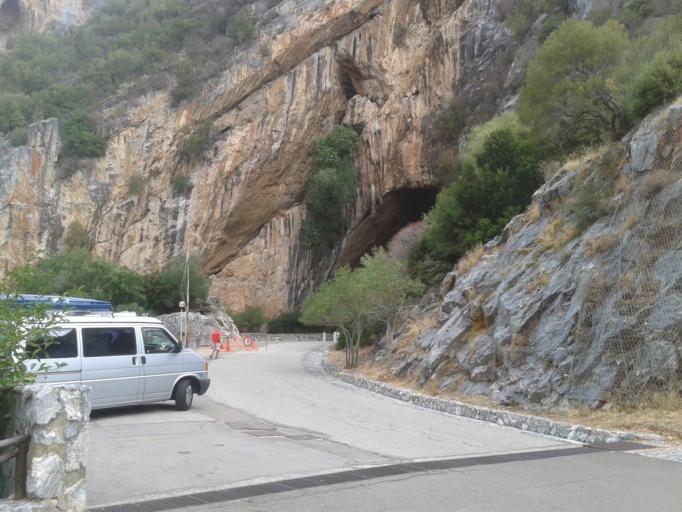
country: IT
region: Sardinia
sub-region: Provincia di Carbonia-Iglesias
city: Domusnovas
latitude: 39.3365
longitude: 8.6278
